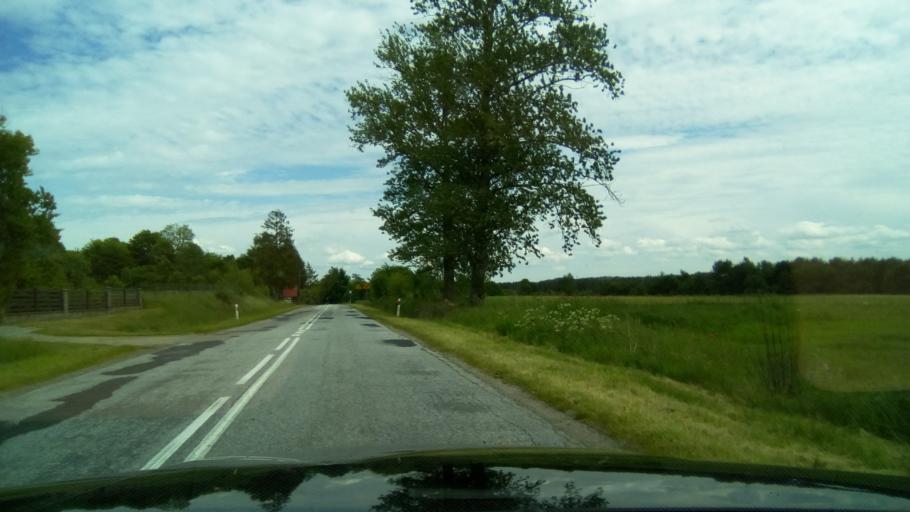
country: PL
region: Pomeranian Voivodeship
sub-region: Powiat bytowski
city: Czarna Dabrowka
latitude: 54.3324
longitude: 17.5250
